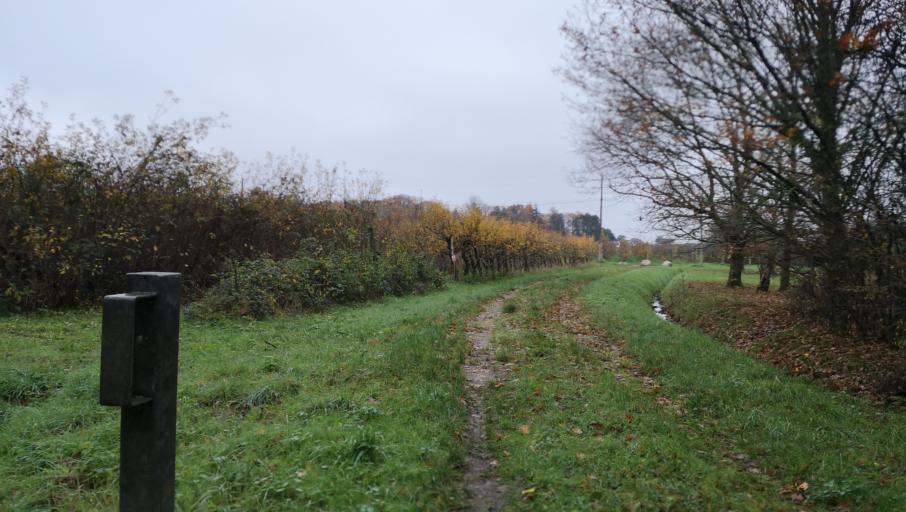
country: FR
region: Centre
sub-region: Departement du Loiret
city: Saint-Jean-de-Braye
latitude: 47.9286
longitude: 1.9814
